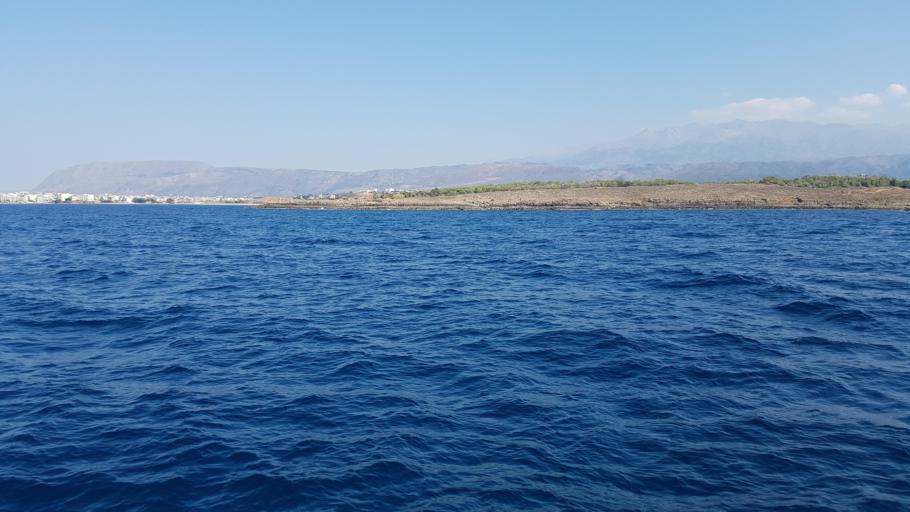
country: GR
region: Crete
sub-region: Nomos Chanias
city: Daratsos
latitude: 35.5215
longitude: 23.9850
